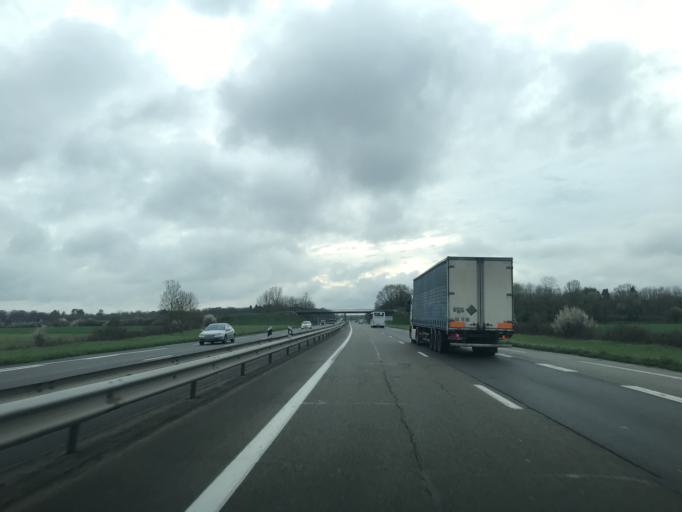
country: FR
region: Centre
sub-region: Departement du Loiret
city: Mardie
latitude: 47.9073
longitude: 2.0564
